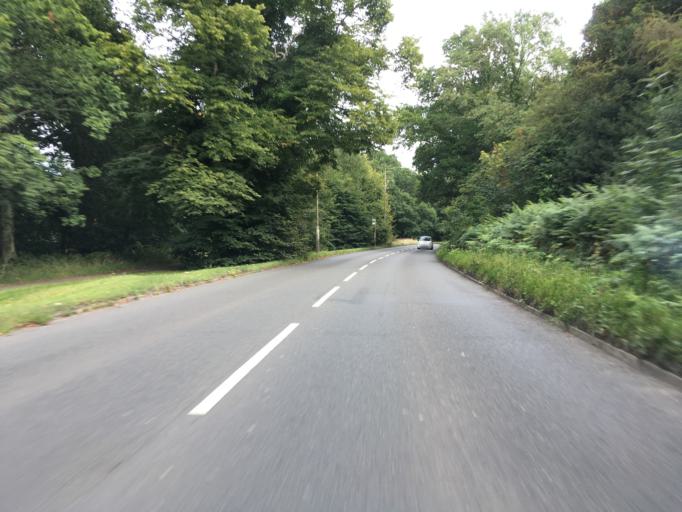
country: GB
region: England
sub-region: Kent
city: Royal Tunbridge Wells
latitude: 51.1322
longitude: 0.2361
